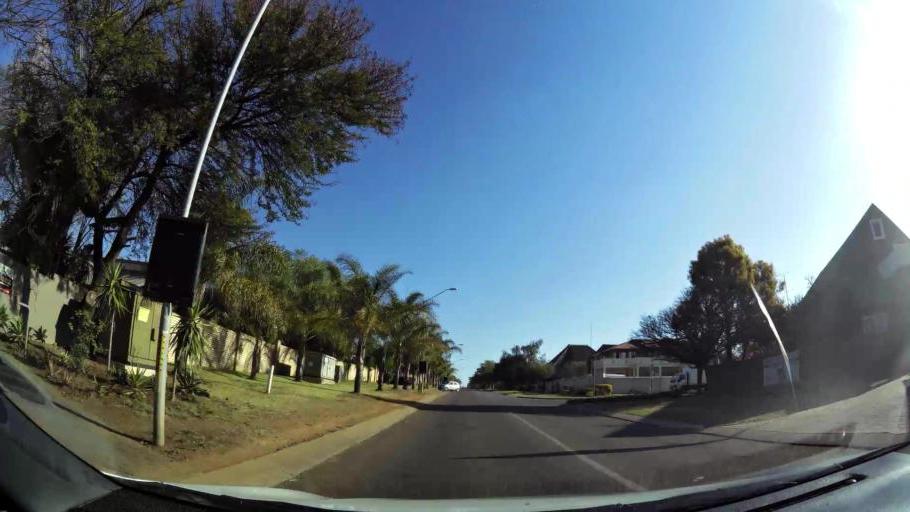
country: ZA
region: Gauteng
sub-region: City of Tshwane Metropolitan Municipality
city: Centurion
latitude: -25.8359
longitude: 28.2966
